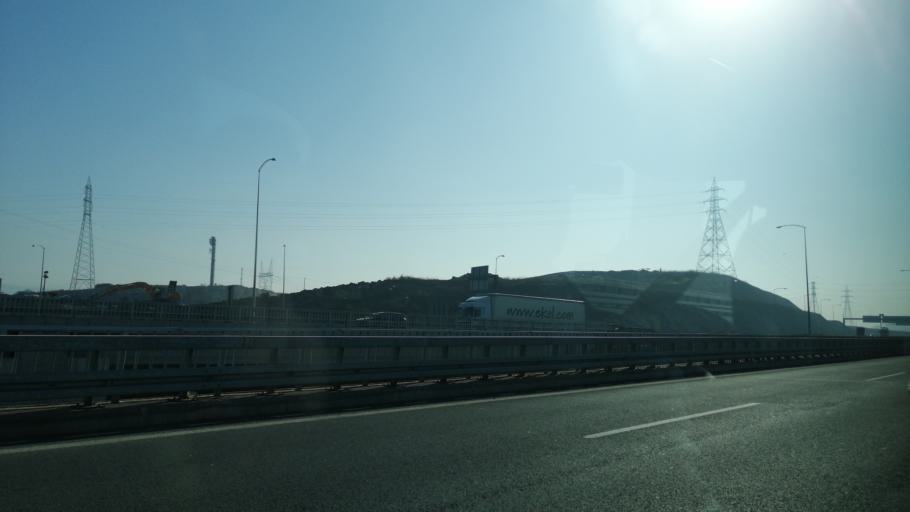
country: TR
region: Kocaeli
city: Tavsanli
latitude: 40.7954
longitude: 29.5100
